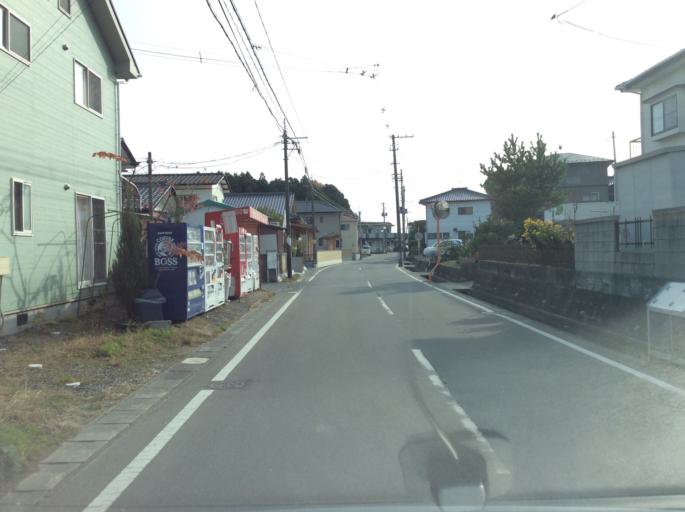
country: JP
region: Fukushima
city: Iwaki
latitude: 37.0723
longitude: 140.9427
